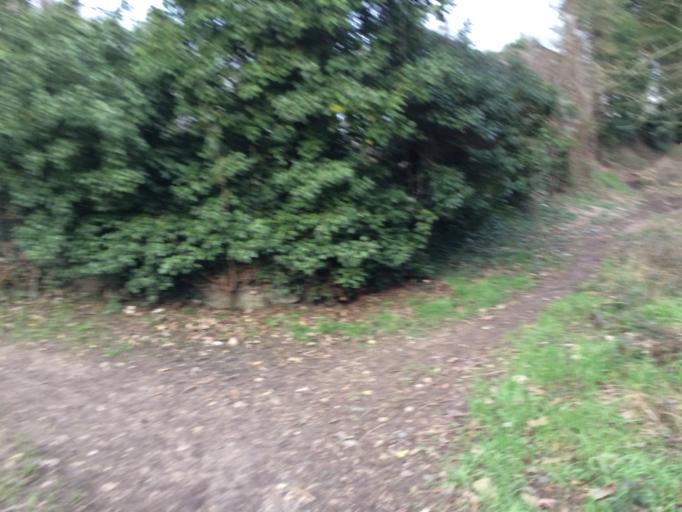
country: FR
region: Ile-de-France
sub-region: Departement de l'Essonne
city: Villemoisson-sur-Orge
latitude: 48.6788
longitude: 2.3305
